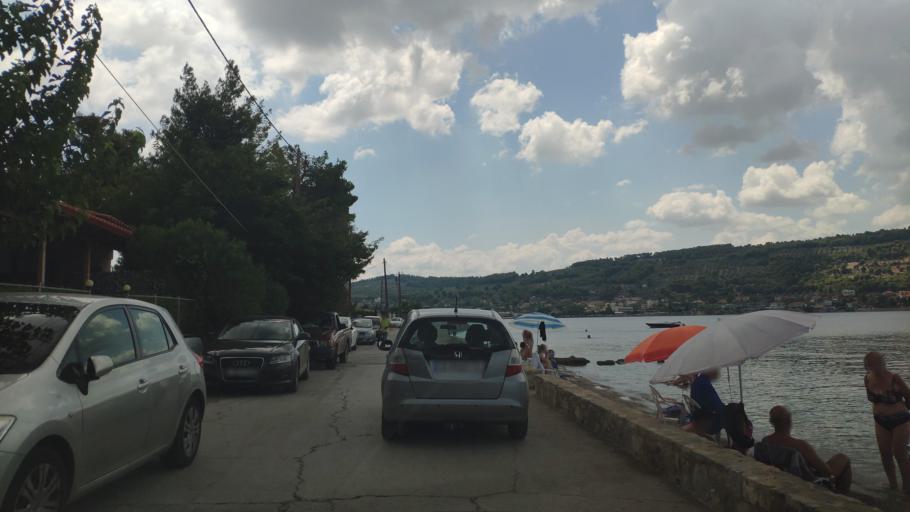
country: GR
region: Central Greece
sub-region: Nomos Fthiotidos
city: Malesina
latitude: 38.6594
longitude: 23.1883
